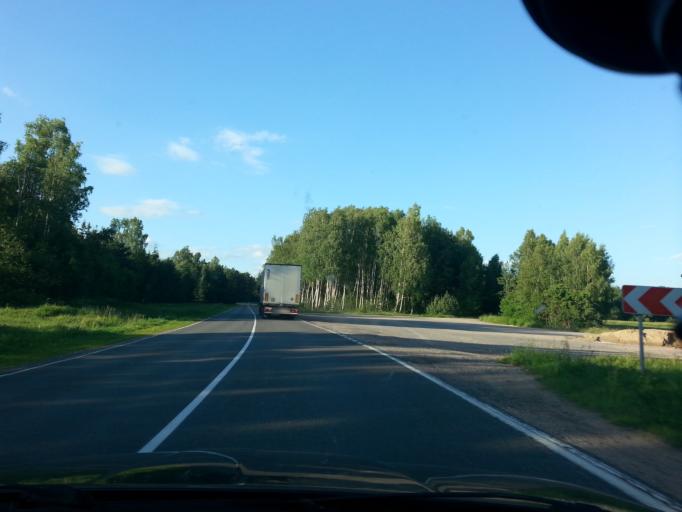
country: BY
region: Minsk
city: Svir
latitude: 54.8808
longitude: 26.3694
